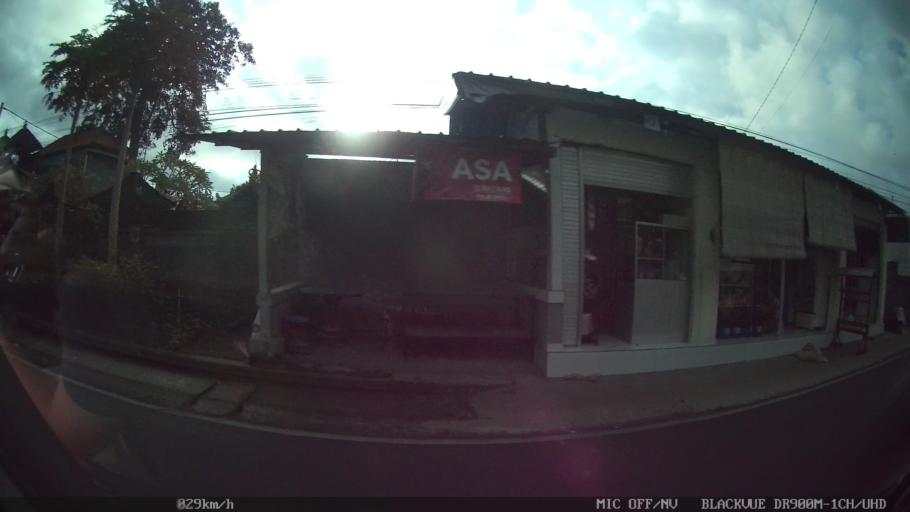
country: ID
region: Bali
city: Banjar Tebongkang
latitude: -8.5226
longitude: 115.2493
